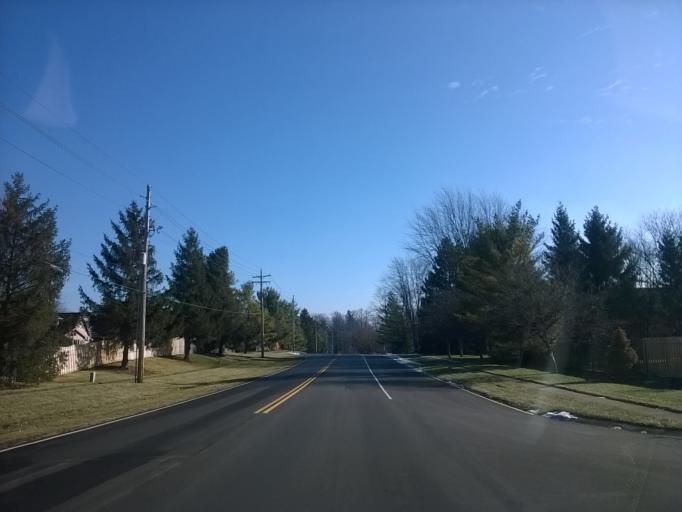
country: US
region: Indiana
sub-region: Hamilton County
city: Carmel
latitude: 39.9857
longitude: -86.0934
